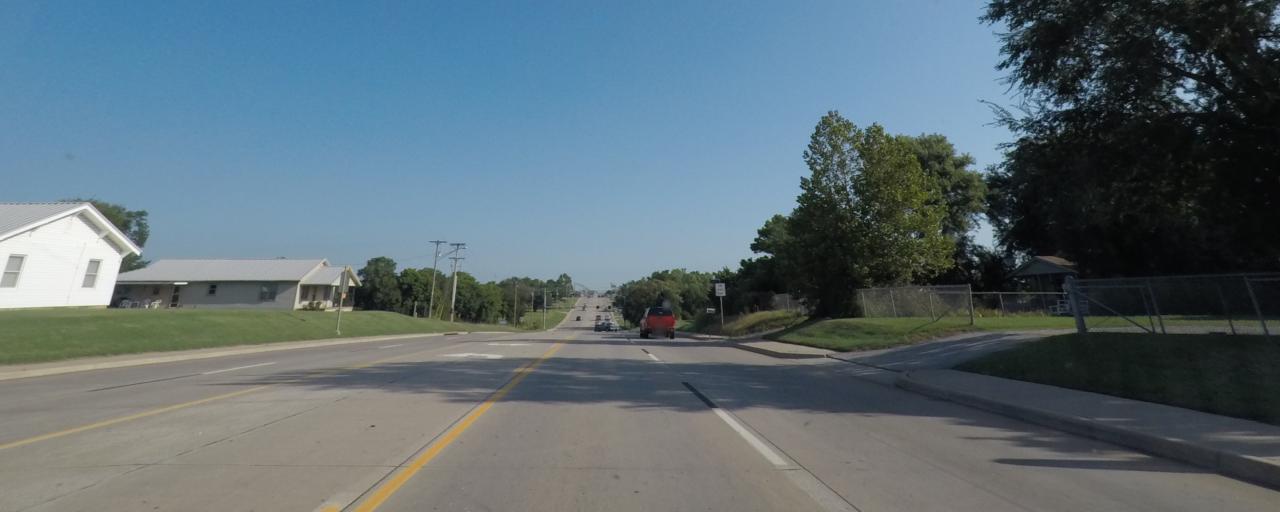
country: US
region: Oklahoma
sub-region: McClain County
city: Newcastle
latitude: 35.2494
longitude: -97.6002
